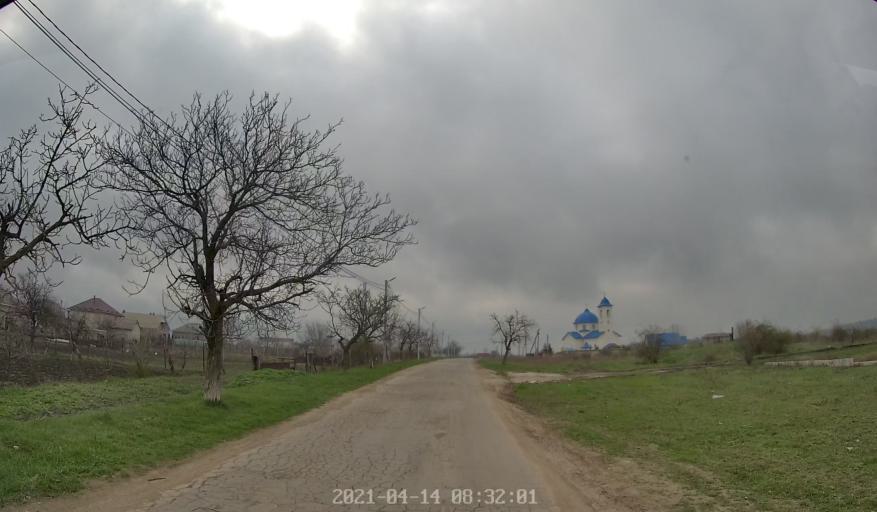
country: MD
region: Chisinau
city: Stauceni
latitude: 47.0601
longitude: 28.9380
